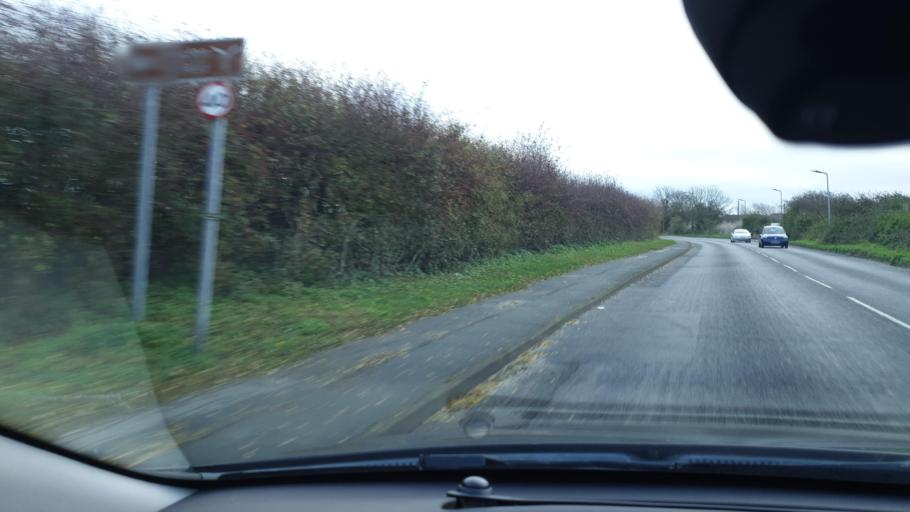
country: GB
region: England
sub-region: Essex
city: Clacton-on-Sea
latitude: 51.7822
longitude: 1.1297
